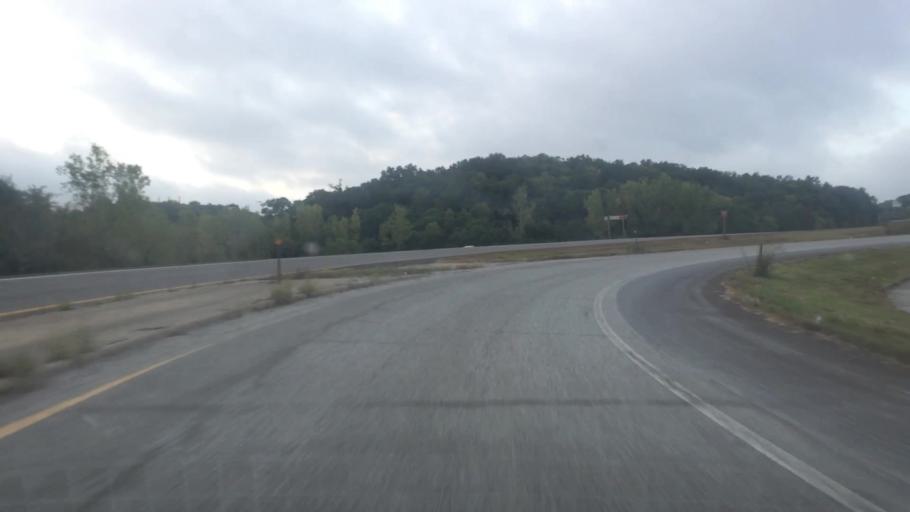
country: US
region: Kansas
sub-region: Wyandotte County
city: Edwardsville
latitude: 39.0411
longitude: -94.7872
